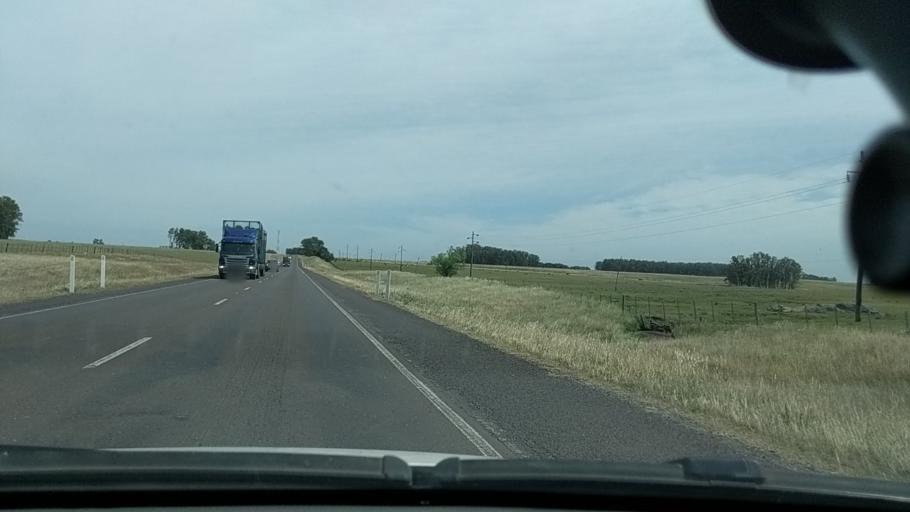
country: UY
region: Durazno
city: Durazno
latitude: -33.5123
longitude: -56.4136
